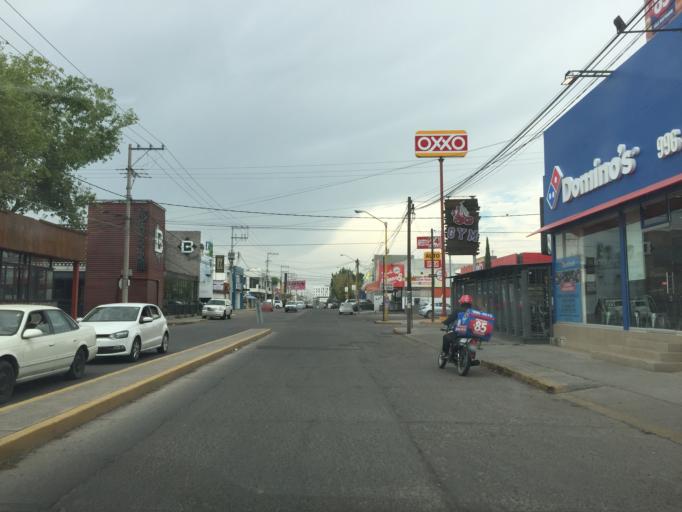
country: MX
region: Aguascalientes
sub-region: Jesus Maria
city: El Llano
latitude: 21.9251
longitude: -102.3048
